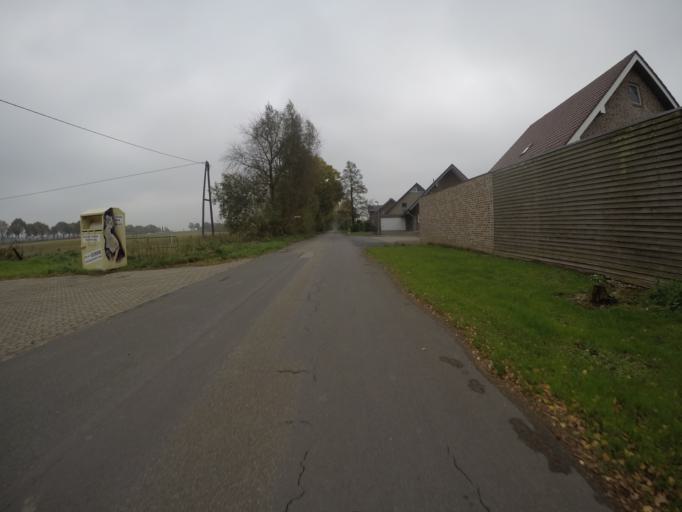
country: DE
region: North Rhine-Westphalia
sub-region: Regierungsbezirk Munster
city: Isselburg
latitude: 51.8230
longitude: 6.5161
